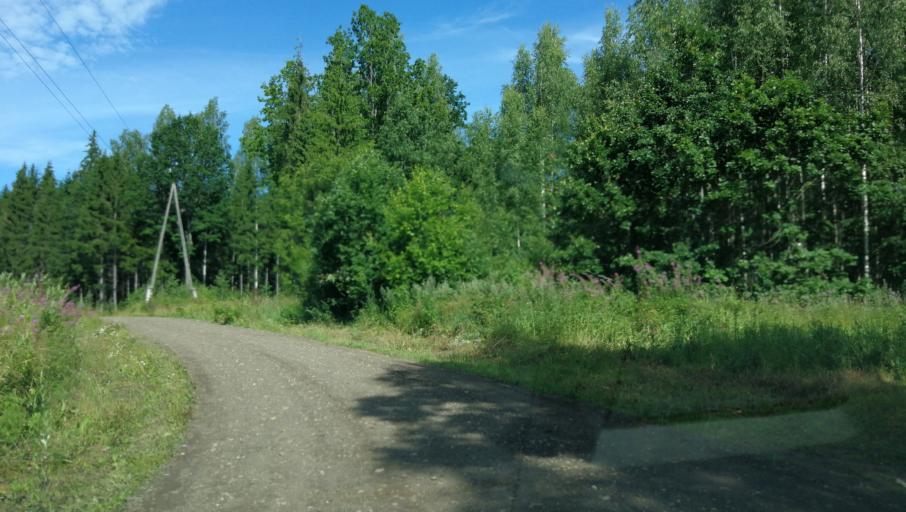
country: LV
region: Gulbenes Rajons
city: Gulbene
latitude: 57.1683
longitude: 26.8717
